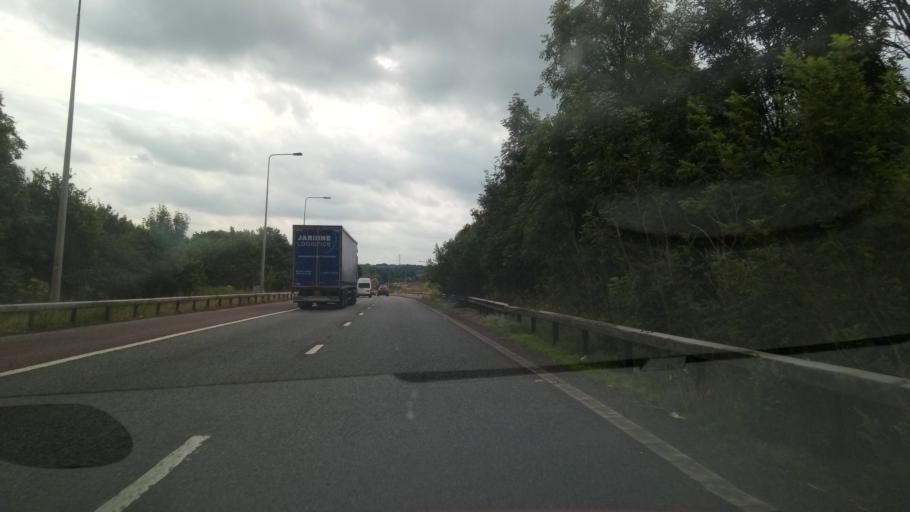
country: GB
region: England
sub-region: Lancashire
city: Clayton-le-Woods
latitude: 53.7330
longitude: -2.6453
